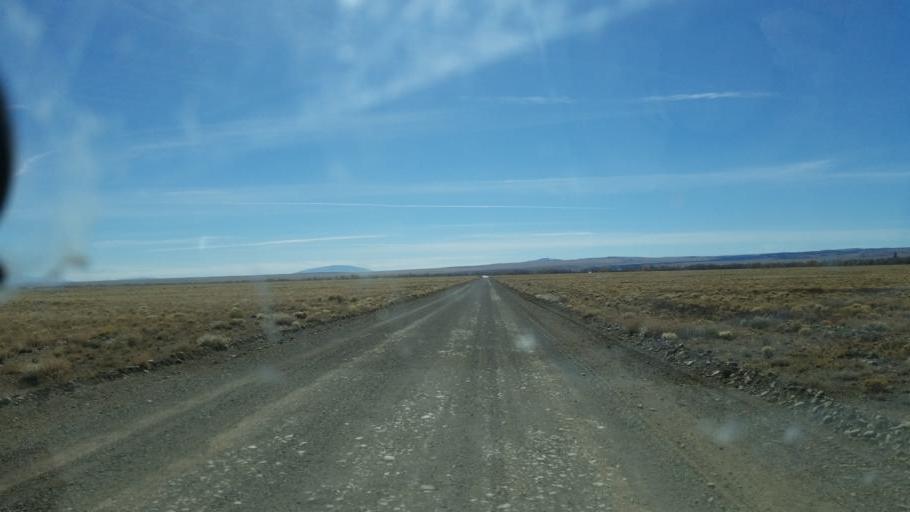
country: US
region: Colorado
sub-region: Rio Grande County
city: Monte Vista
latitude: 37.3232
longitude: -106.1488
